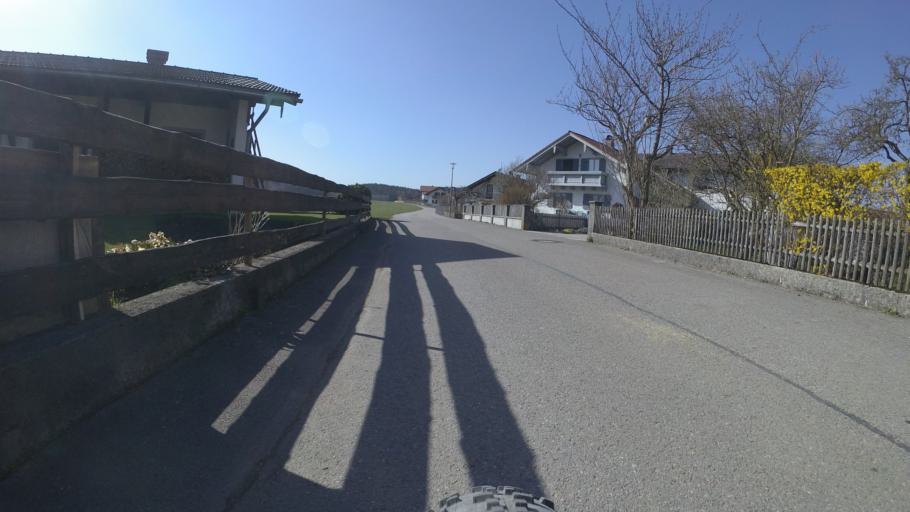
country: DE
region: Bavaria
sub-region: Upper Bavaria
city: Nussdorf
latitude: 47.9221
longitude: 12.6123
